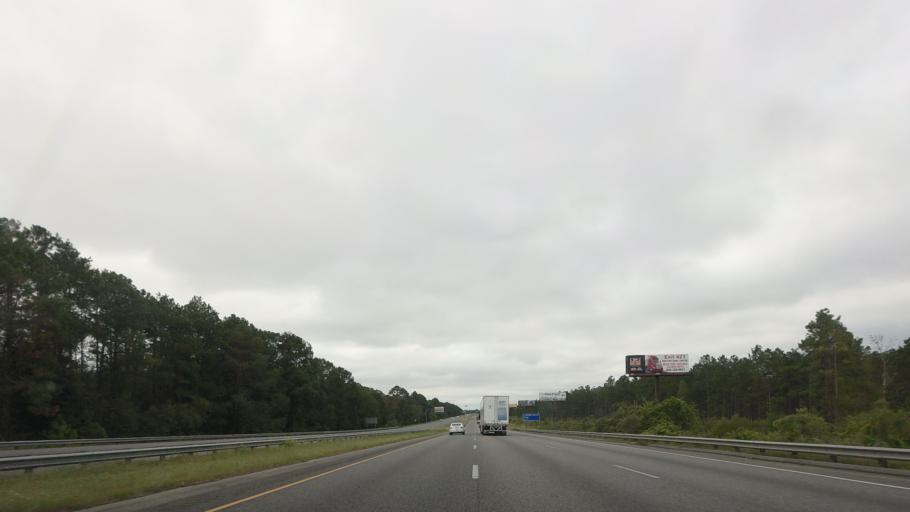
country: US
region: Georgia
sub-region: Lowndes County
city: Valdosta
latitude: 30.7702
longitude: -83.2905
